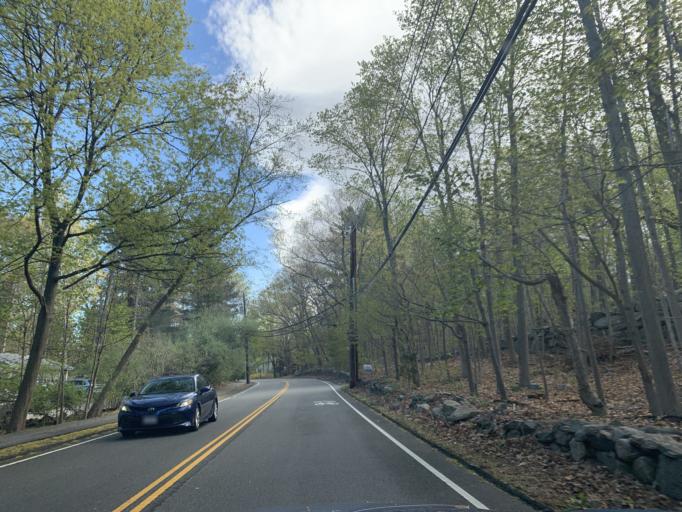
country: US
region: Massachusetts
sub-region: Norfolk County
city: Milton
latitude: 42.2352
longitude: -71.1081
